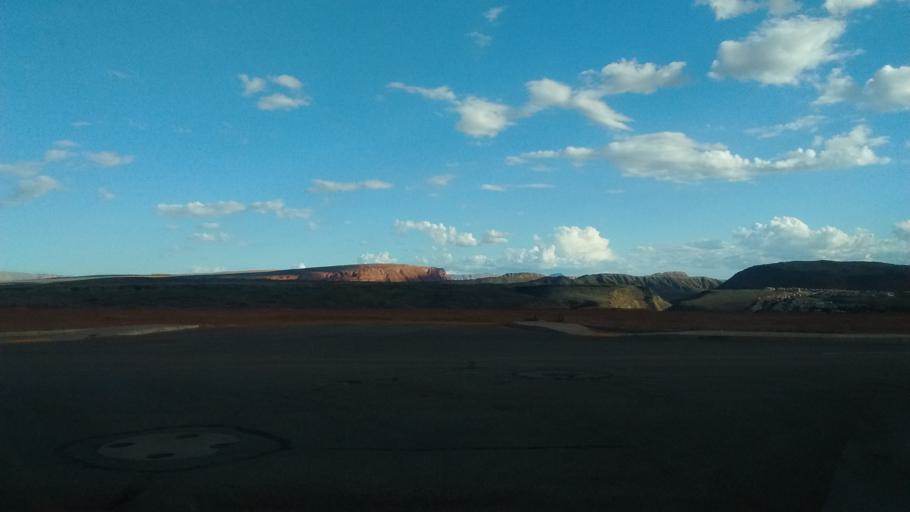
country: US
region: Utah
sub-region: Washington County
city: Washington
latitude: 37.1439
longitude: -113.4887
